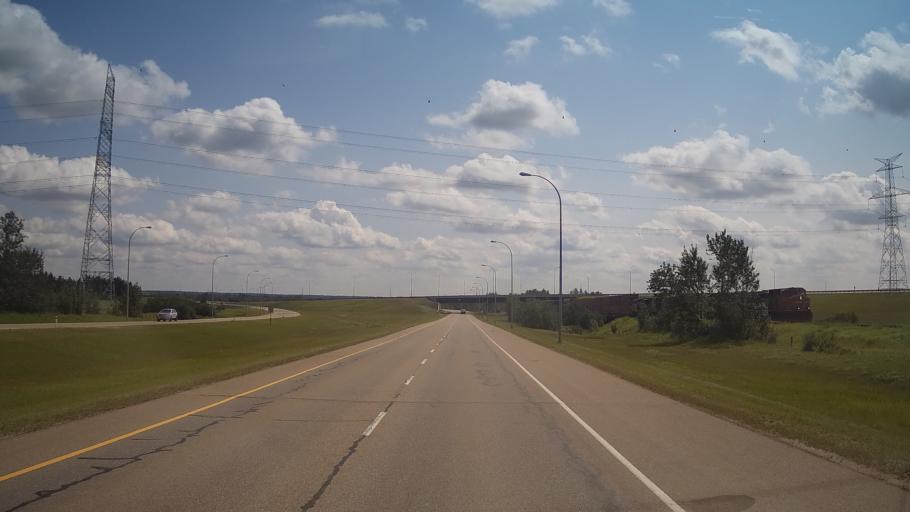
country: CA
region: Alberta
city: Sherwood Park
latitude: 53.4530
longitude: -113.3399
